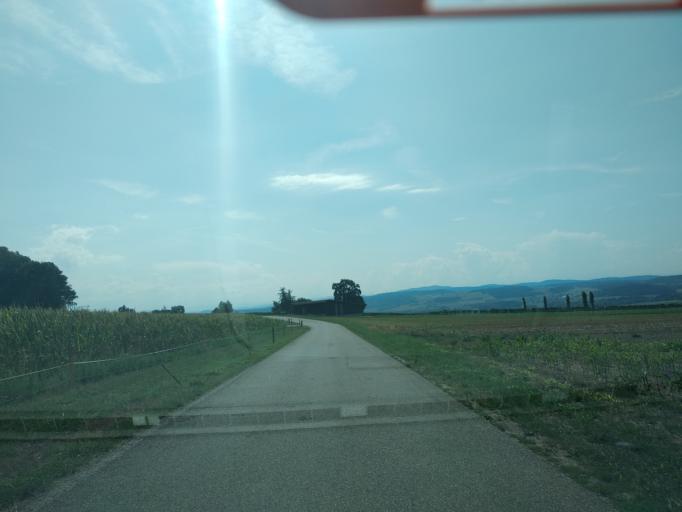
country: CH
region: Thurgau
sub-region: Frauenfeld District
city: Huttwilen
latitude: 47.5893
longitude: 8.8220
